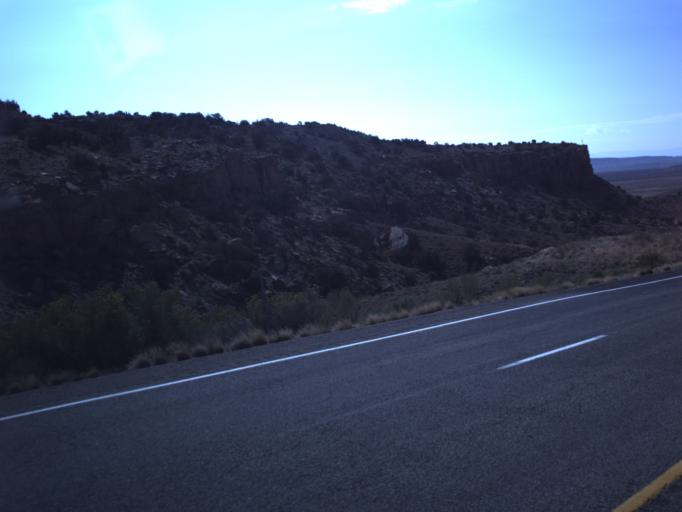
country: US
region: Utah
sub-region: San Juan County
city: Blanding
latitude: 37.4308
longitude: -109.4714
